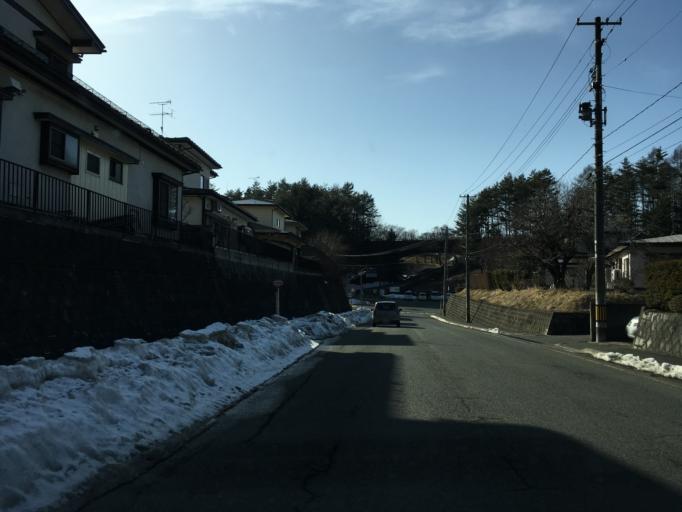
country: JP
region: Iwate
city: Morioka-shi
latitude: 39.7542
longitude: 141.1562
